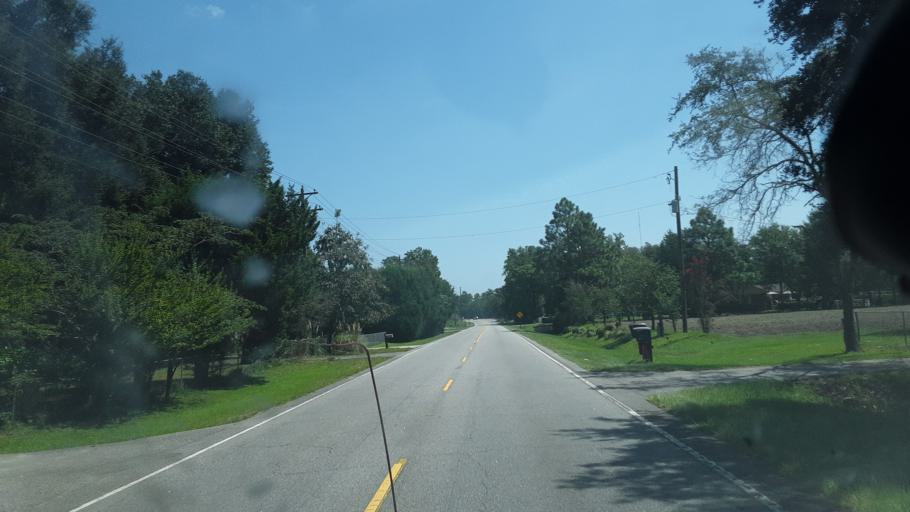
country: US
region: South Carolina
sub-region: Horry County
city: Red Hill
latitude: 33.8219
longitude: -78.9084
